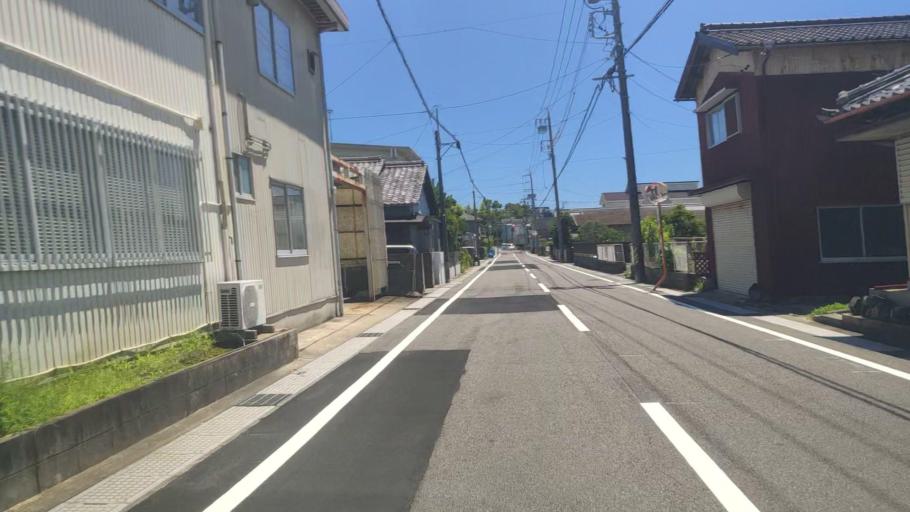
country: JP
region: Mie
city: Suzuka
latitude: 34.8548
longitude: 136.5869
